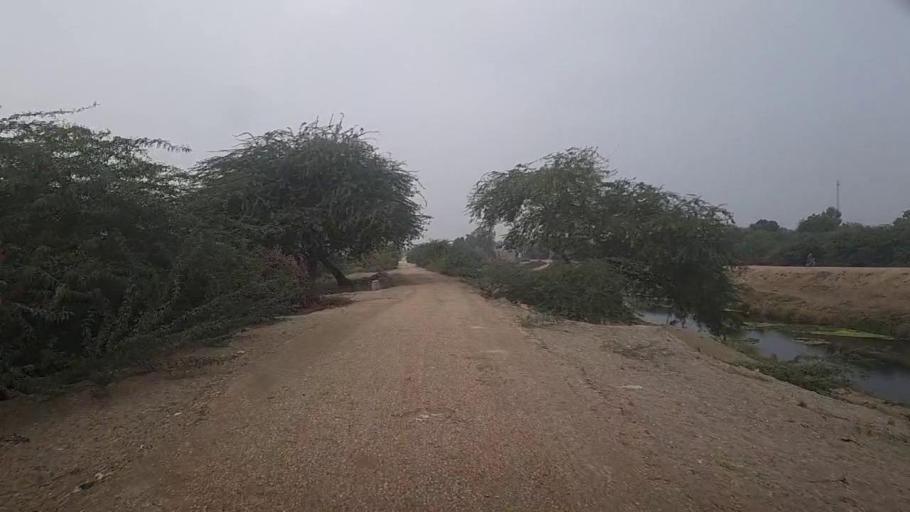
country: PK
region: Sindh
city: Gambat
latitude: 27.3600
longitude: 68.5677
